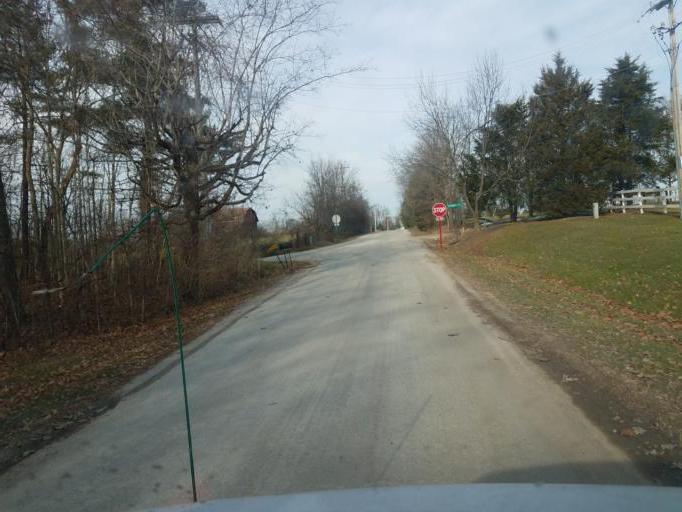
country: US
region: Ohio
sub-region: Delaware County
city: Ashley
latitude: 40.3837
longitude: -82.9363
